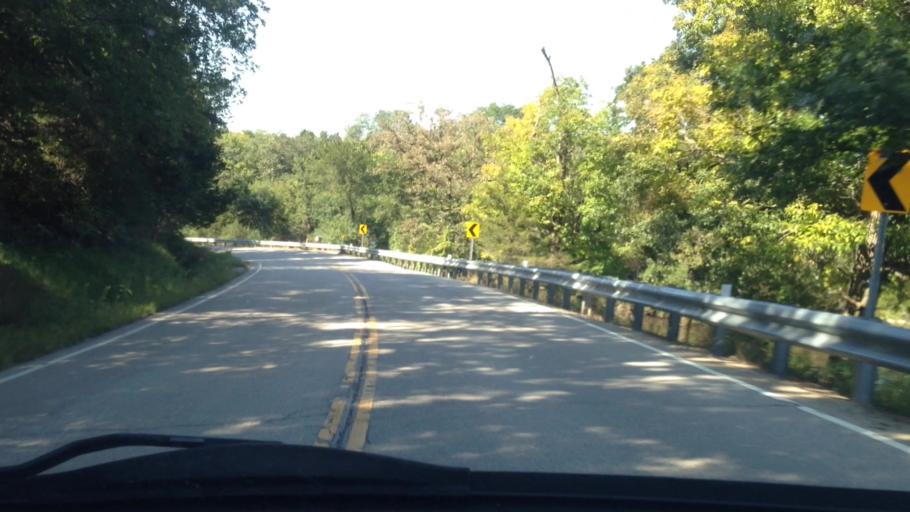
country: US
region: Minnesota
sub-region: Fillmore County
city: Rushford
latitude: 43.6481
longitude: -91.7872
